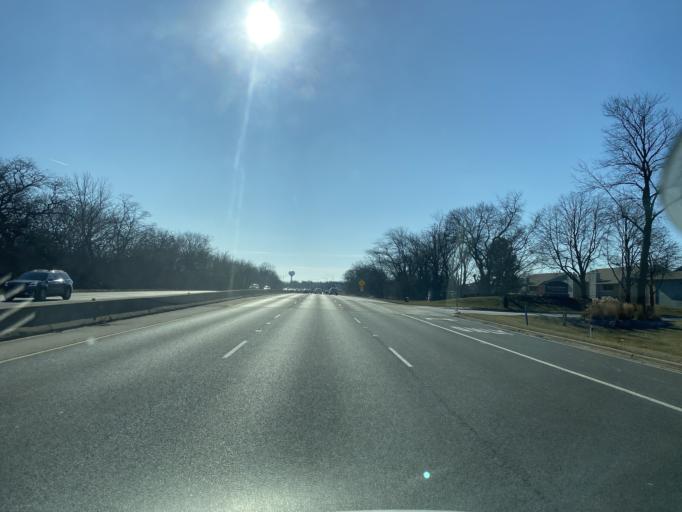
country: US
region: Illinois
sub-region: DuPage County
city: Willowbrook
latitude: 41.7796
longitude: -87.9469
